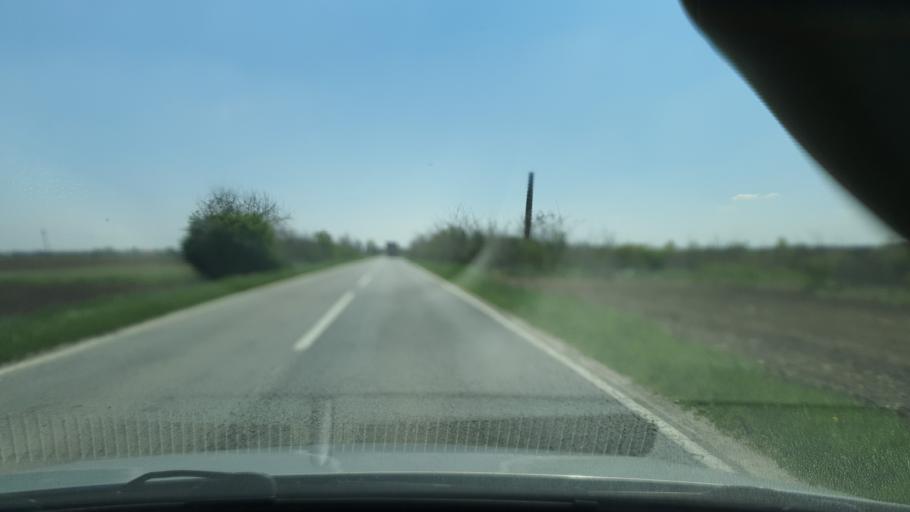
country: RS
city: Doroslovo
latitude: 45.5727
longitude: 19.1922
